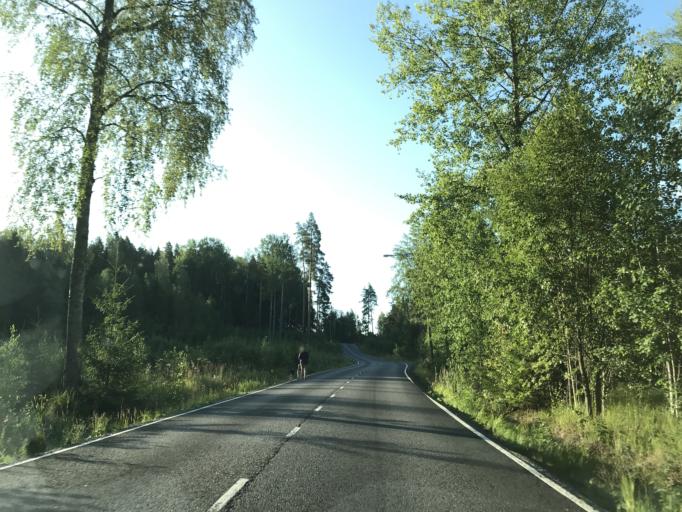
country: FI
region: Uusimaa
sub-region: Helsinki
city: Kauniainen
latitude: 60.3565
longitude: 24.6874
